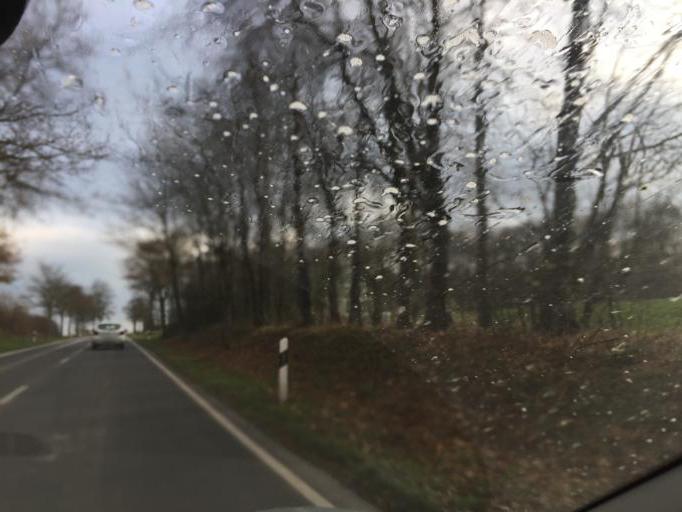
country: LU
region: Diekirch
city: Bettborn
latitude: 49.7707
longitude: 5.9246
